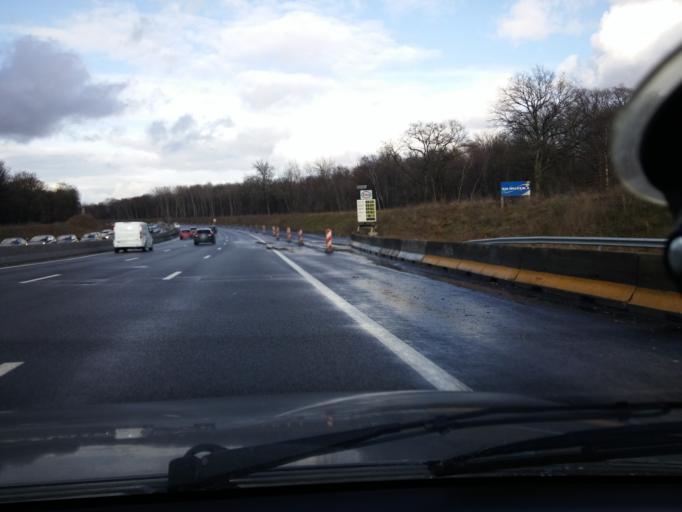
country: FR
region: Ile-de-France
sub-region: Departement de Seine-et-Marne
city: Emerainville
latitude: 48.8048
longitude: 2.6284
